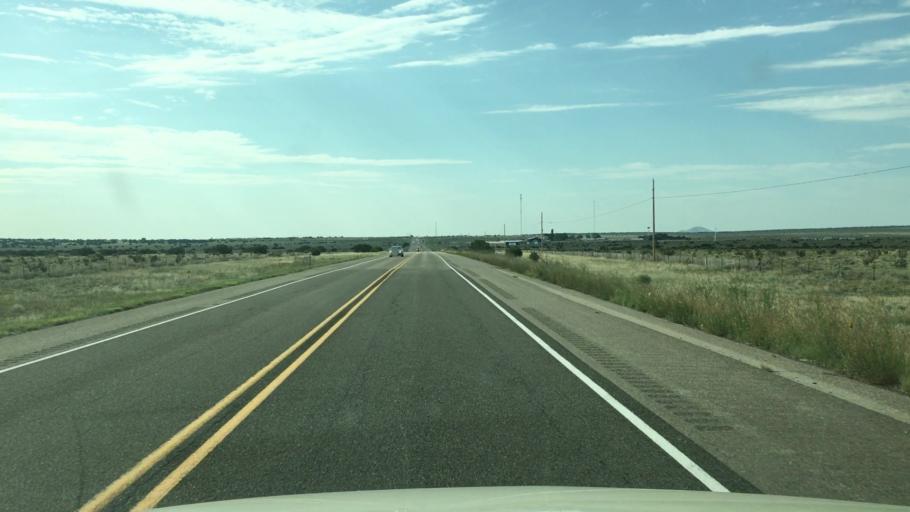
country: US
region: New Mexico
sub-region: Torrance County
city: Moriarty
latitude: 35.0261
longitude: -105.6743
